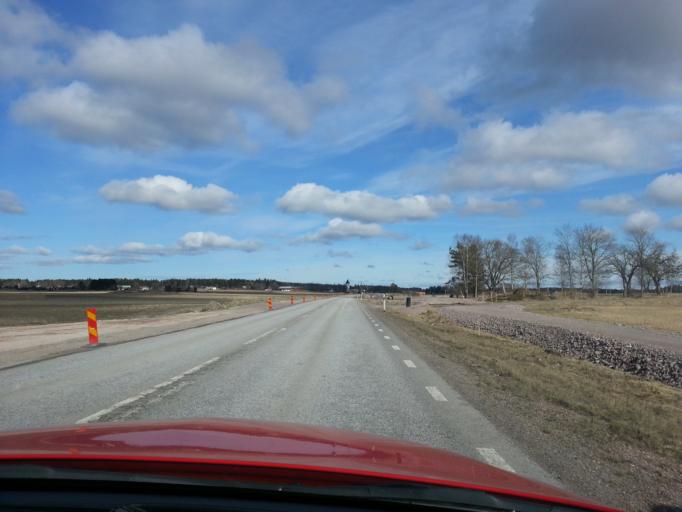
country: SE
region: Uppsala
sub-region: Osthammars Kommun
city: Gimo
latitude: 60.0499
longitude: 18.0514
